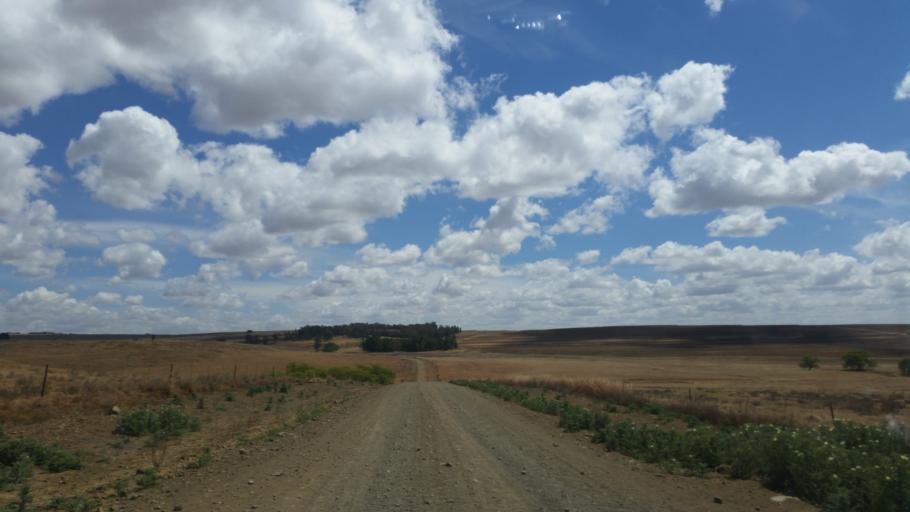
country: ZA
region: Orange Free State
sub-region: Thabo Mofutsanyana District Municipality
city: Bethlehem
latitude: -28.1916
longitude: 28.5922
